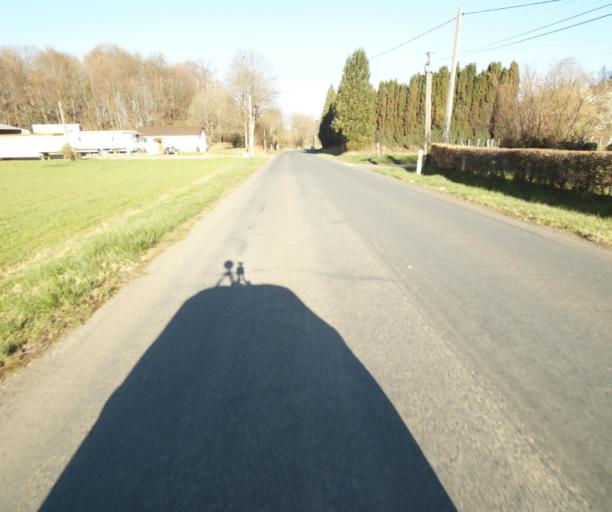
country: FR
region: Limousin
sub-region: Departement de la Correze
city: Uzerche
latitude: 45.3879
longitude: 1.6013
